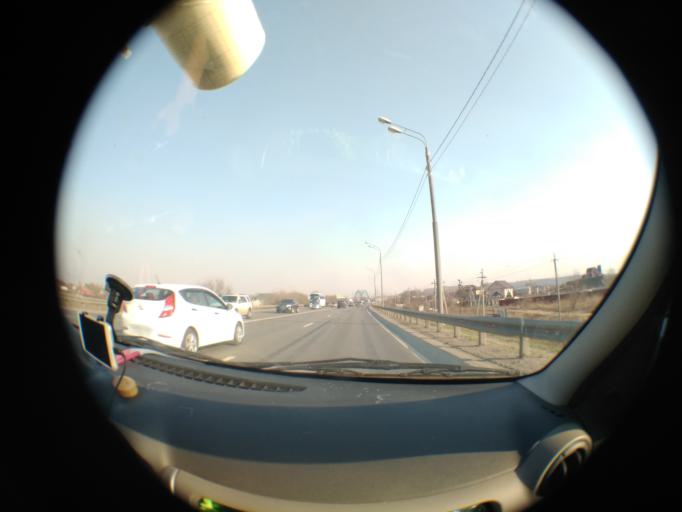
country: RU
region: Moskovskaya
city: Ostrovtsy
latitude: 55.5744
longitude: 38.0269
